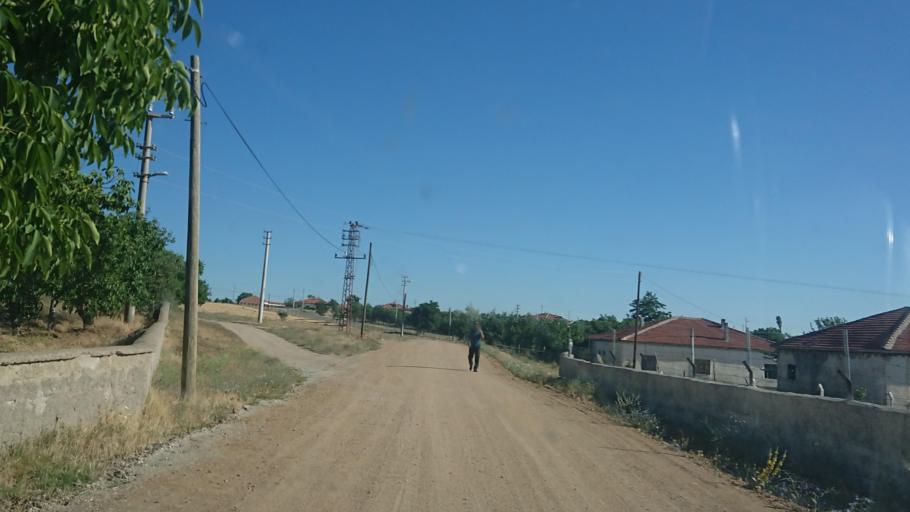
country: TR
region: Aksaray
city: Agacoren
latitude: 38.8755
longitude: 33.9524
